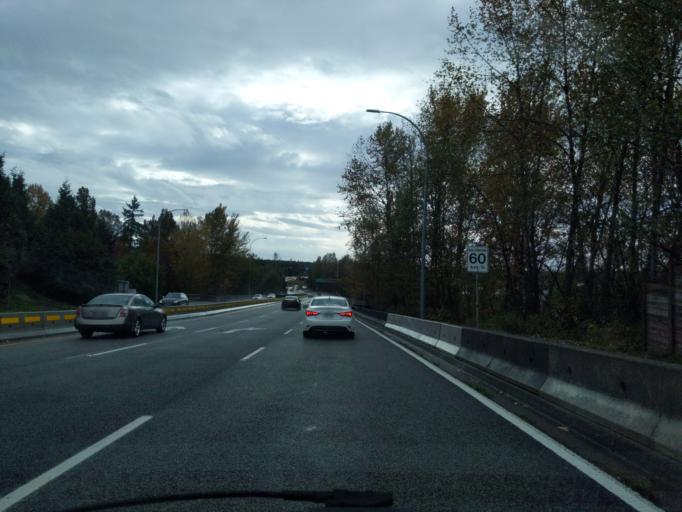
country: CA
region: British Columbia
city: Delta
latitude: 49.1516
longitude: -122.9351
